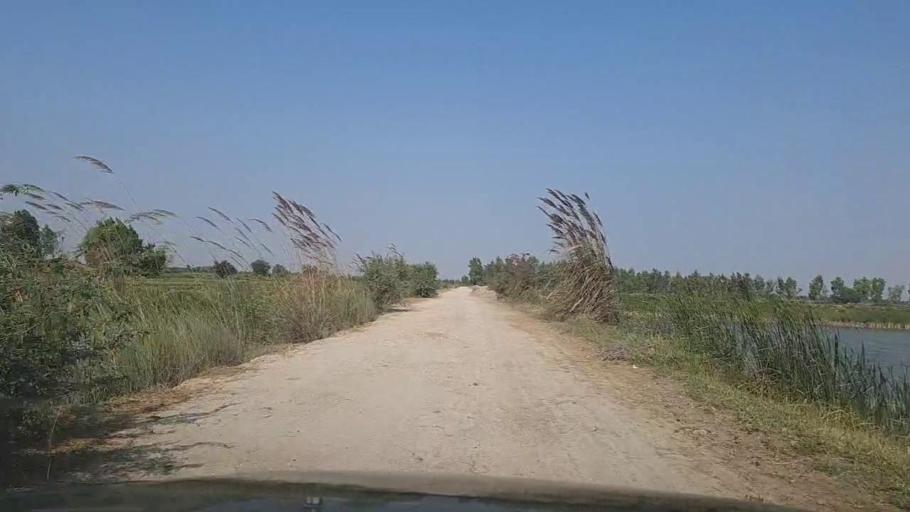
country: PK
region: Sindh
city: Thatta
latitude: 24.6203
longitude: 67.8154
